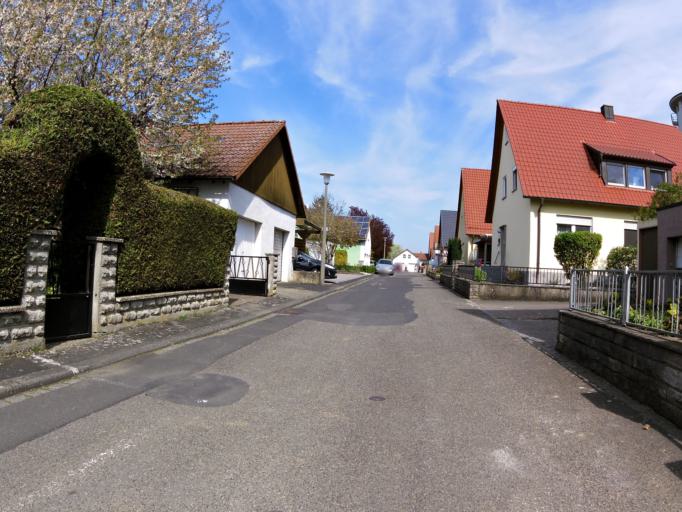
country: DE
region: Bavaria
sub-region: Regierungsbezirk Unterfranken
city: Unterpleichfeld
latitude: 49.8720
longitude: 10.0341
